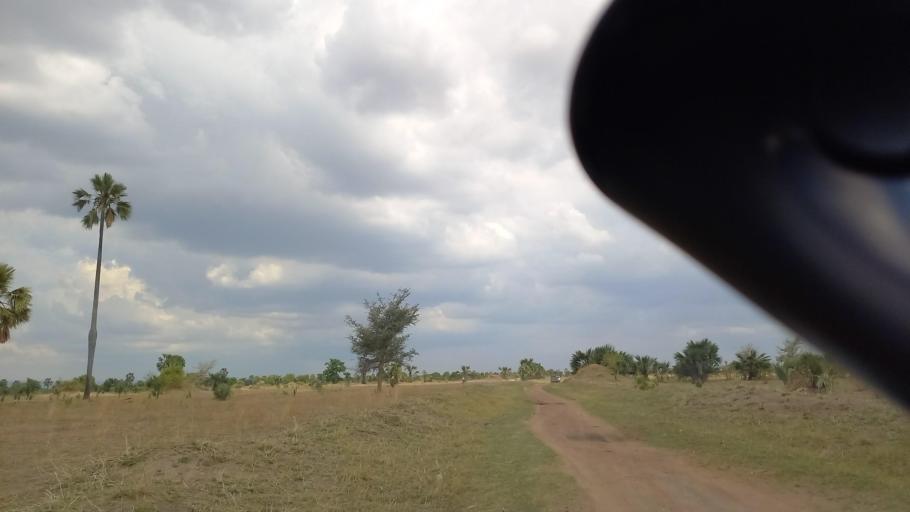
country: ZM
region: Lusaka
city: Kafue
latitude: -15.8286
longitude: 28.0578
